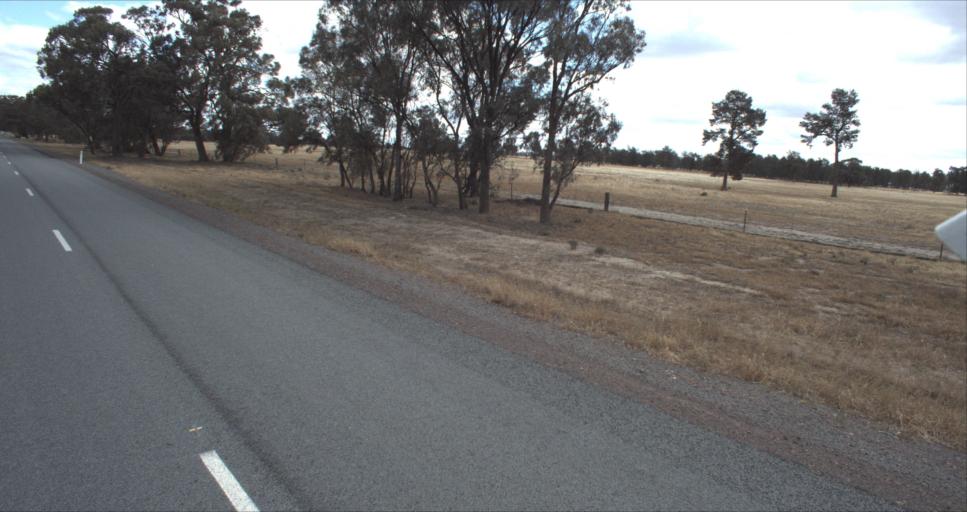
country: AU
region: New South Wales
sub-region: Leeton
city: Leeton
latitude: -34.6829
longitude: 146.3452
